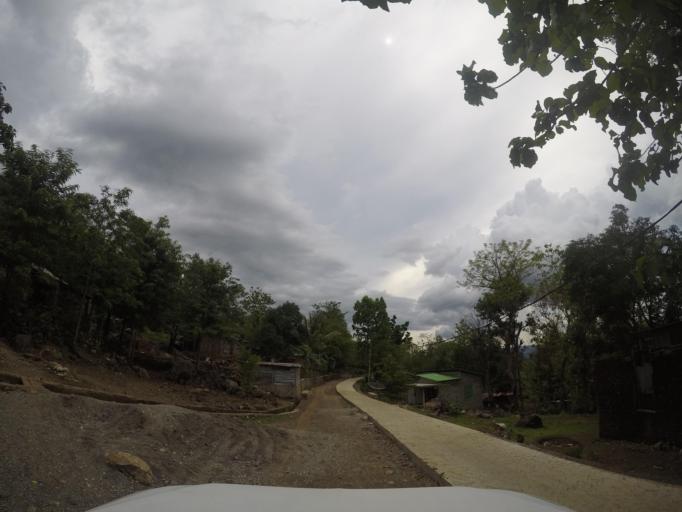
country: TL
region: Bobonaro
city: Maliana
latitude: -8.9963
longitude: 125.2136
